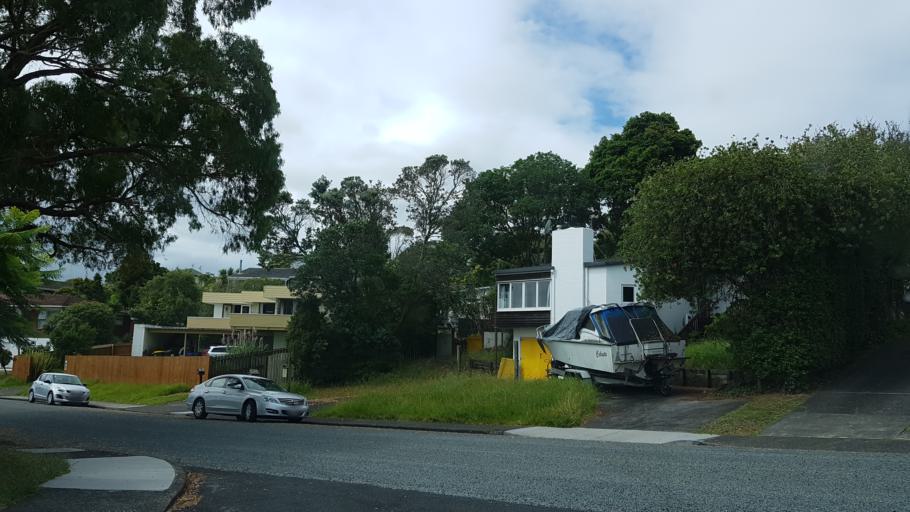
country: NZ
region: Auckland
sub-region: Auckland
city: North Shore
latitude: -36.7766
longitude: 174.7099
